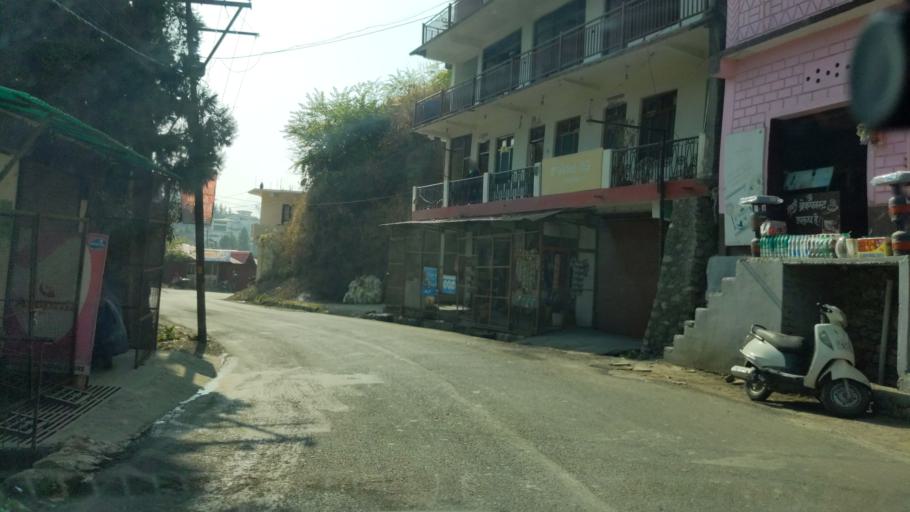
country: IN
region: Uttarakhand
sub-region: Naini Tal
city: Bhowali
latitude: 29.3852
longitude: 79.5279
